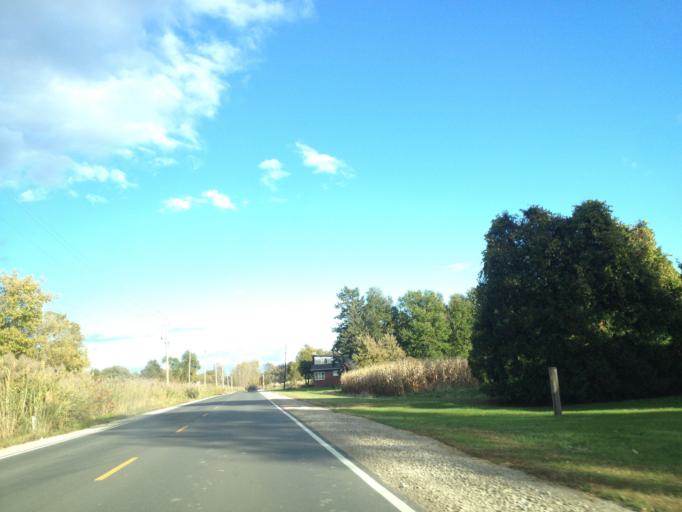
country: US
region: Michigan
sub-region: Wayne County
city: Grosse Pointe Farms
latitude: 42.2972
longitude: -82.6755
